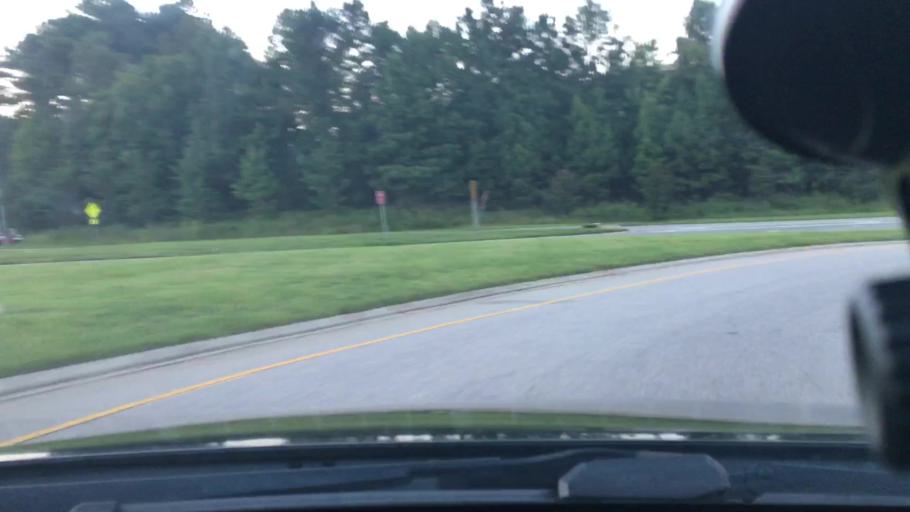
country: US
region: North Carolina
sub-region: Wake County
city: Cary
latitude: 35.7494
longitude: -78.7725
